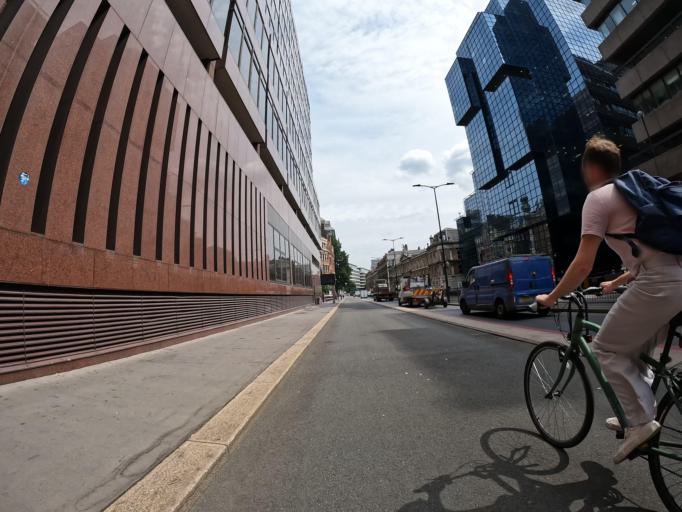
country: GB
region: England
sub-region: Greater London
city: City of Westminster
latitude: 51.4998
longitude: -0.1217
